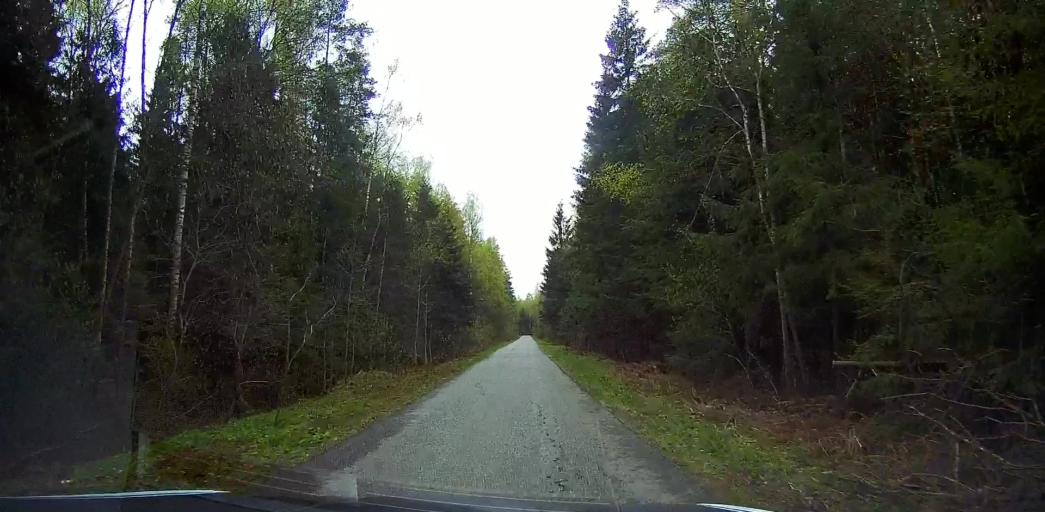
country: RU
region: Moskovskaya
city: Malyshevo
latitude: 55.5400
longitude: 38.3851
